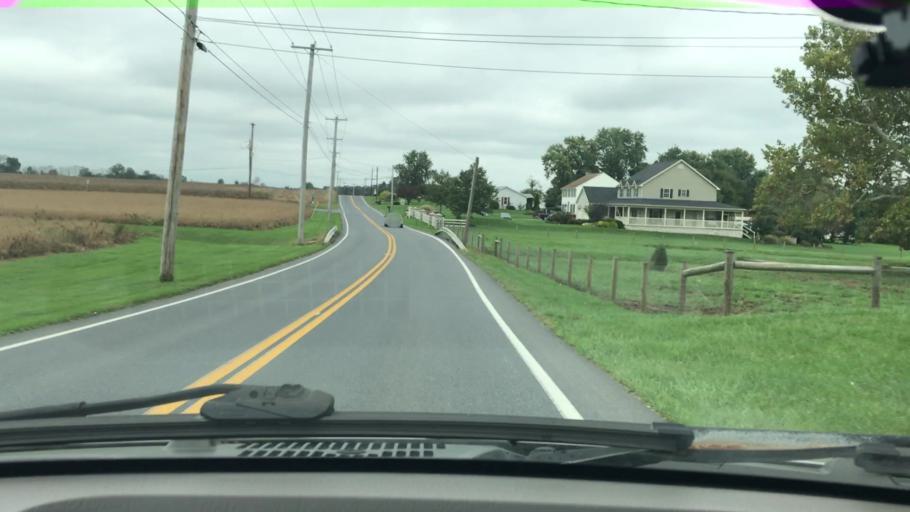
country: US
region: Pennsylvania
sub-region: Lancaster County
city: Maytown
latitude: 40.0915
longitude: -76.5584
